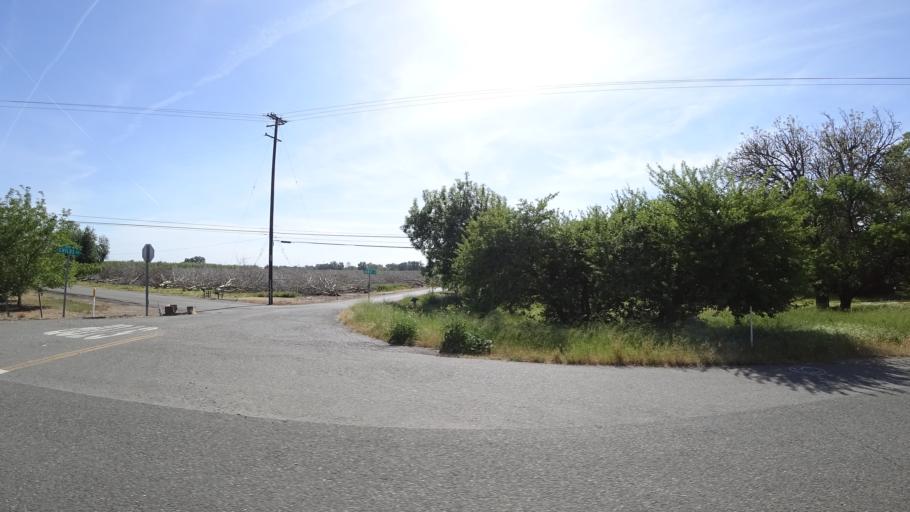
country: US
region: California
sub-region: Tehama County
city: Gerber
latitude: 40.1140
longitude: -122.1171
